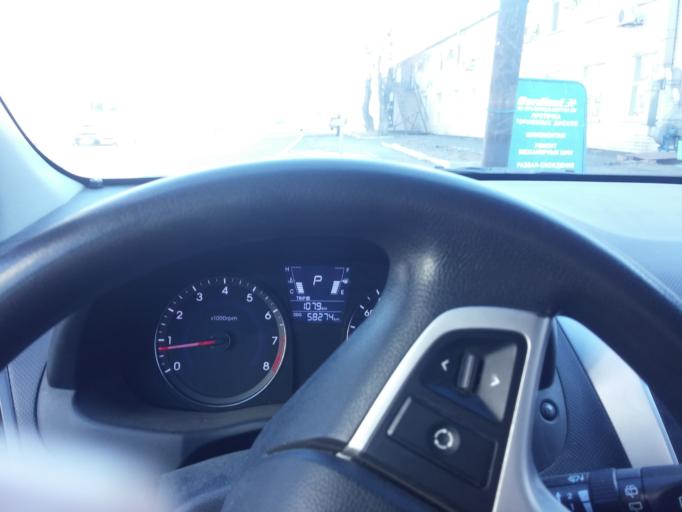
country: RU
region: Khabarovsk Krai
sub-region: Khabarovskiy Rayon
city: Khabarovsk
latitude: 48.4613
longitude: 135.0954
